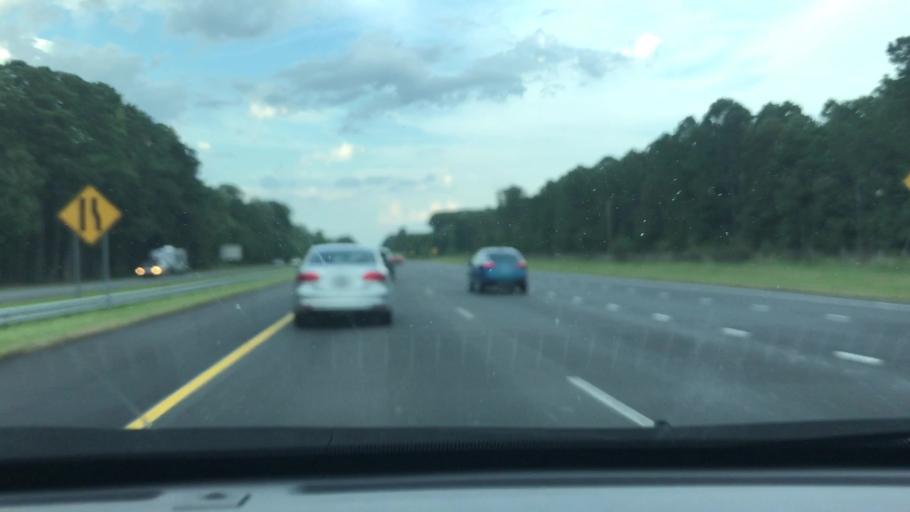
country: US
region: North Carolina
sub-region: Cumberland County
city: Eastover
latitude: 35.1296
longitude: -78.7473
